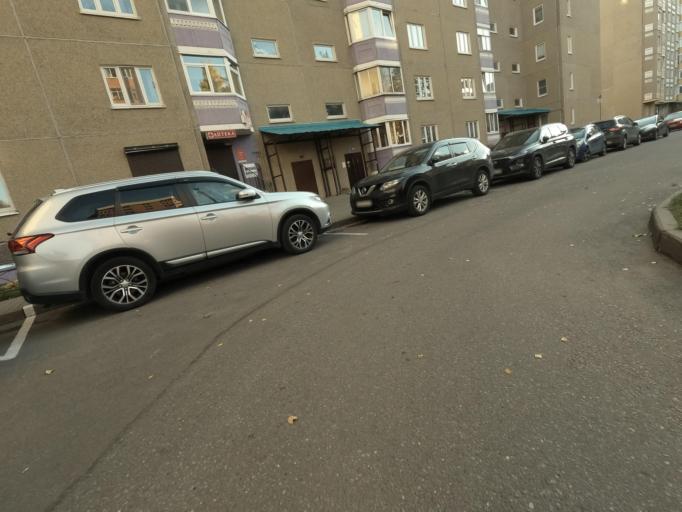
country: RU
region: Leningrad
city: Sertolovo
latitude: 60.1434
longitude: 30.2306
